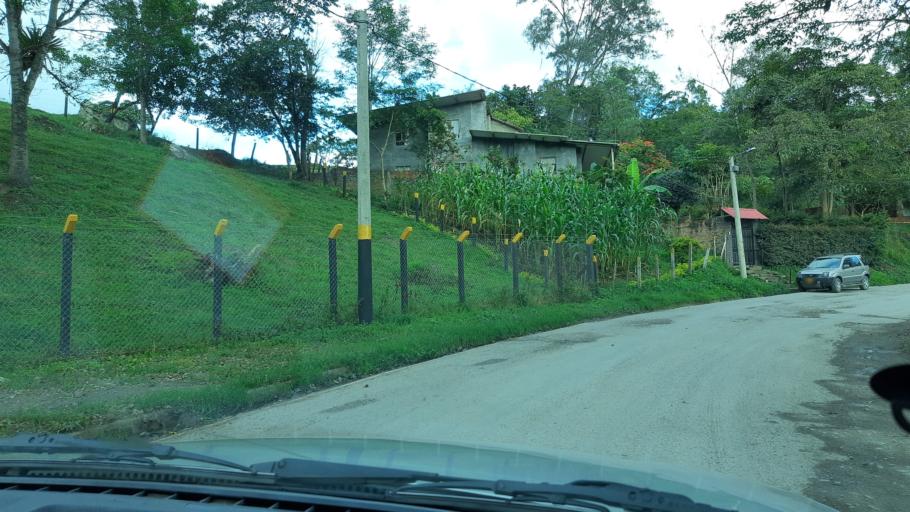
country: CO
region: Boyaca
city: Garagoa
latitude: 5.0896
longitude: -73.3661
